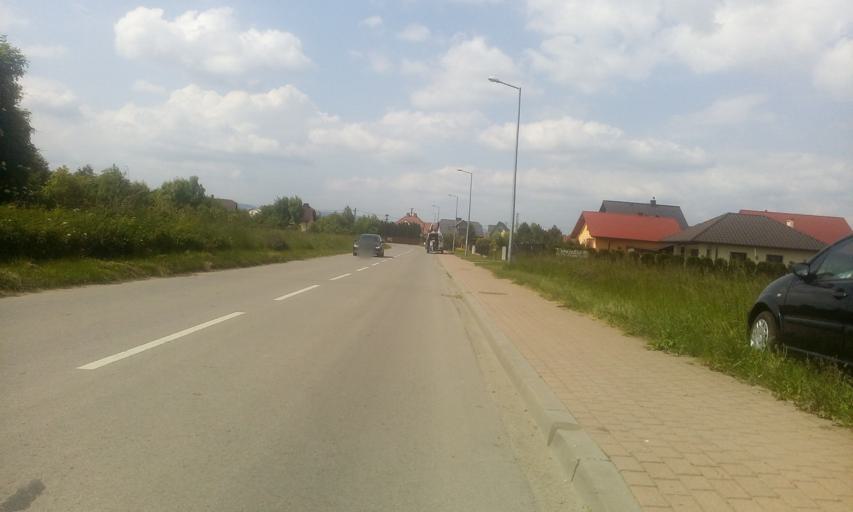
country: PL
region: Lesser Poland Voivodeship
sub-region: Powiat nowosadecki
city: Stary Sacz
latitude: 49.5677
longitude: 20.6386
